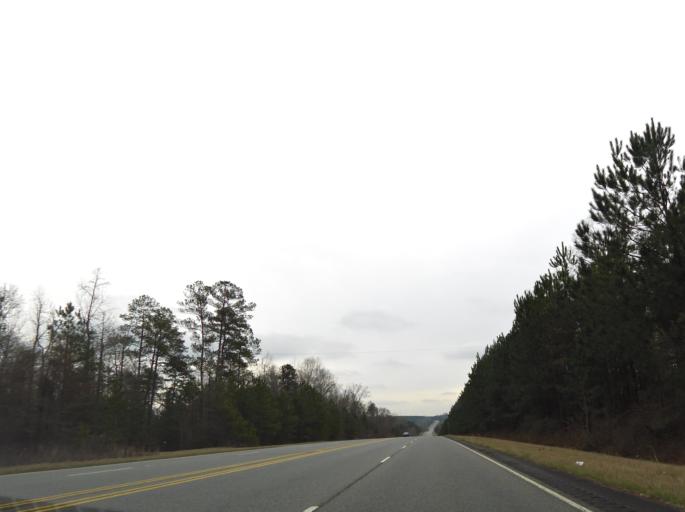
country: US
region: Georgia
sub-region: Bleckley County
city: Cochran
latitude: 32.5210
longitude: -83.4351
